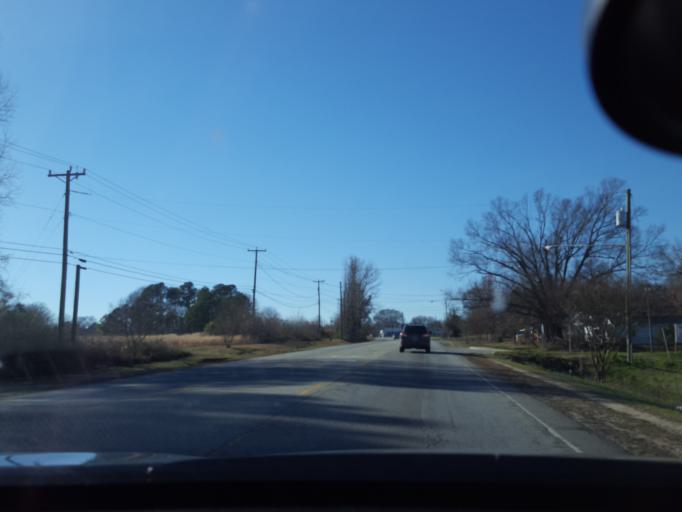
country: US
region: North Carolina
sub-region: Halifax County
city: Roanoke Rapids
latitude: 36.4412
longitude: -77.6647
